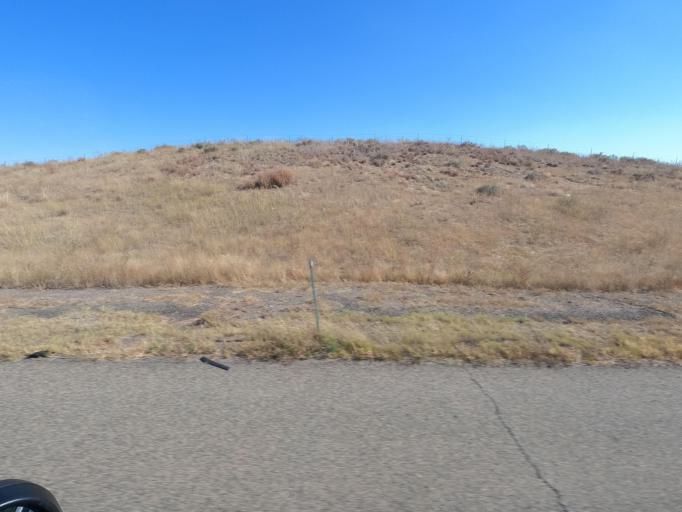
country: US
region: Colorado
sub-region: Logan County
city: Sterling
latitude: 40.6360
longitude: -103.1564
